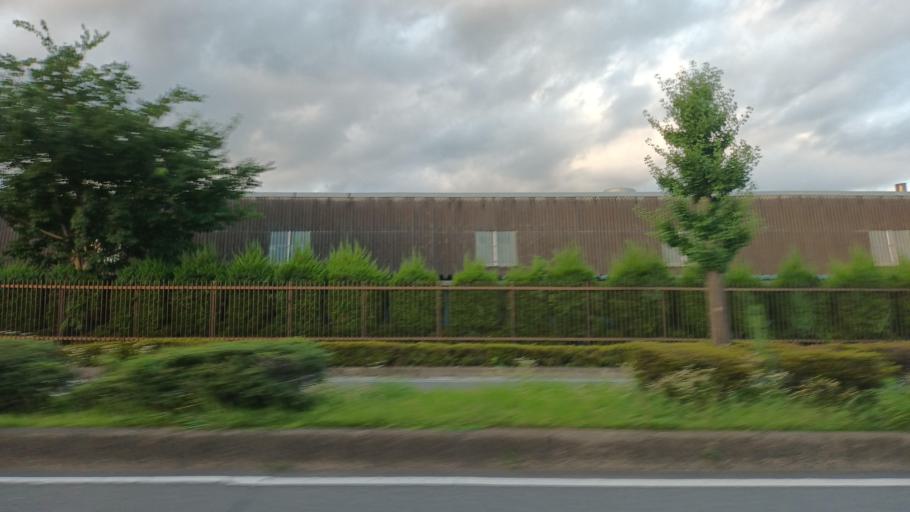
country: JP
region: Tokyo
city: Fussa
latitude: 35.7717
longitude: 139.3155
